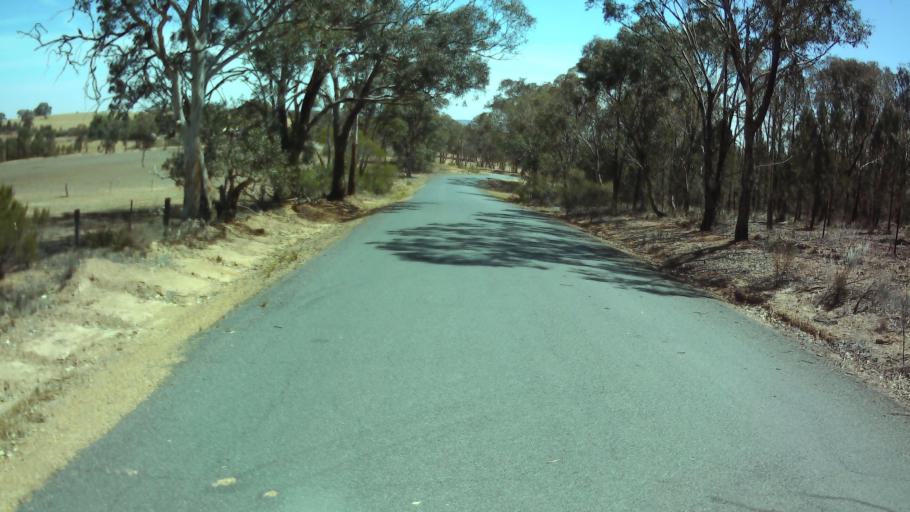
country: AU
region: New South Wales
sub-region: Weddin
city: Grenfell
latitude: -33.9071
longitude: 148.1803
